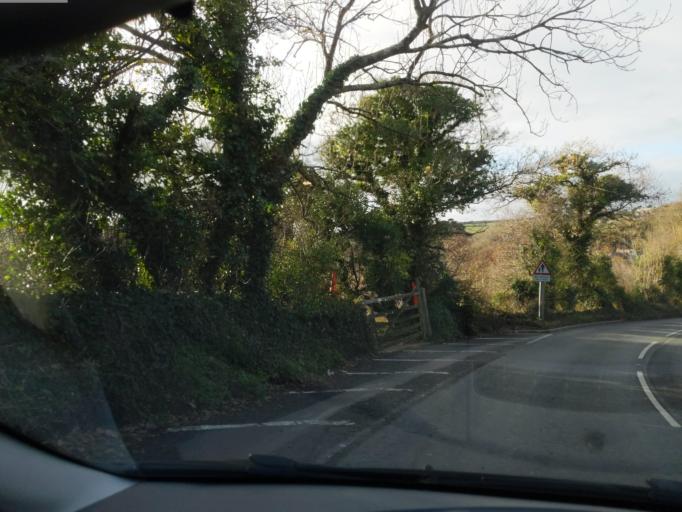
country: GB
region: England
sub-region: Cornwall
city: Padstow
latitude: 50.5112
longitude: -4.9342
